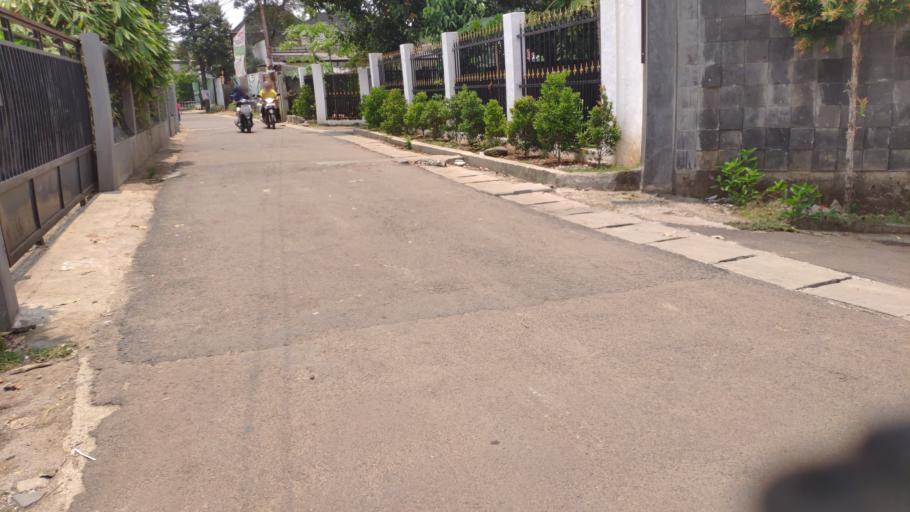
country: ID
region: West Java
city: Pamulang
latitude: -6.3340
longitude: 106.7947
